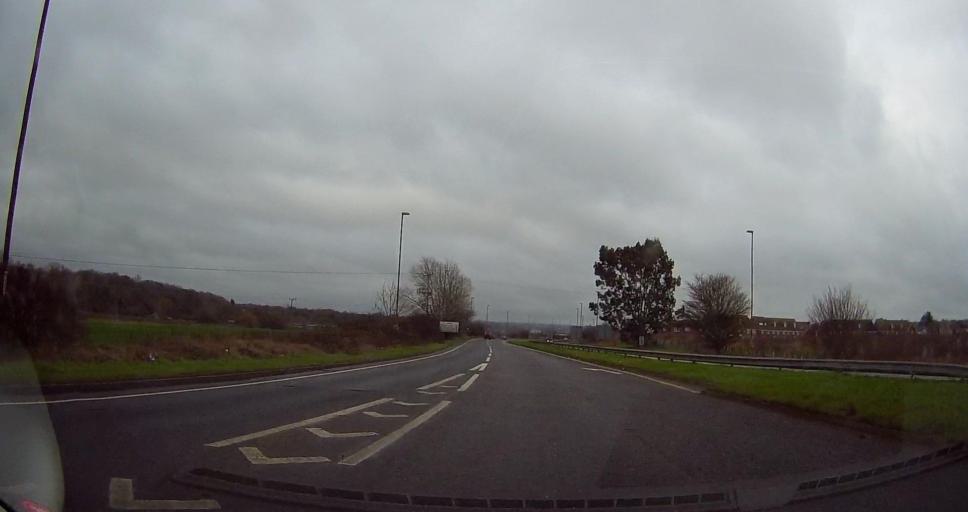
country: GB
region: England
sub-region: Medway
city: Rochester
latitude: 51.4138
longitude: 0.5174
